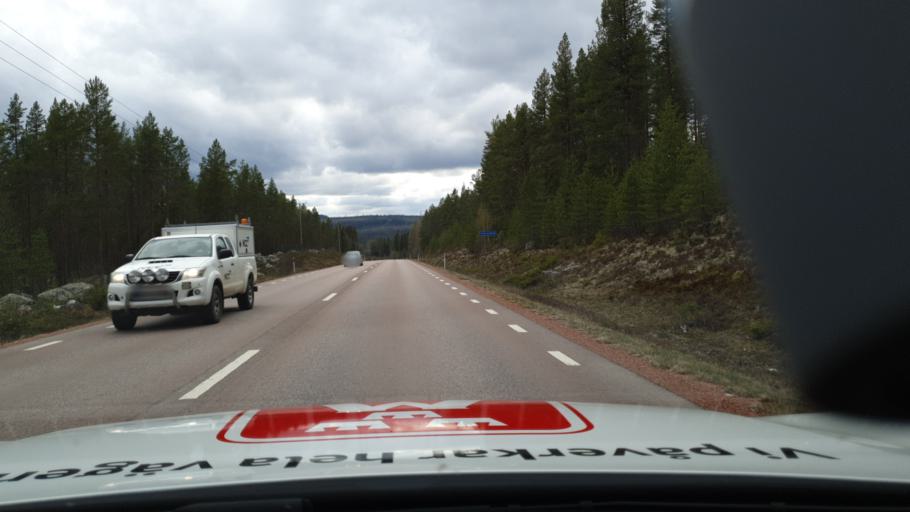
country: SE
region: Jaemtland
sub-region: Ragunda Kommun
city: Hammarstrand
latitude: 63.1720
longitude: 15.8342
